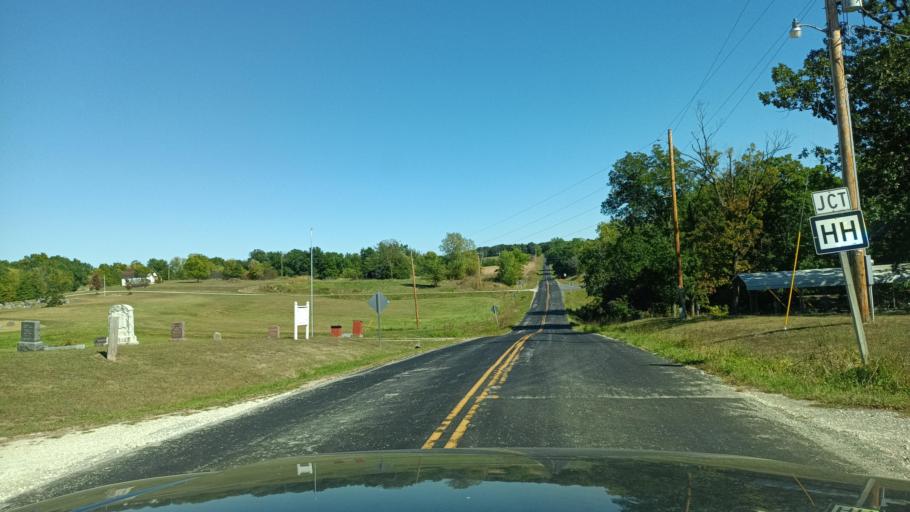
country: US
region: Missouri
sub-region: Macon County
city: La Plata
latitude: 39.9537
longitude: -92.6459
